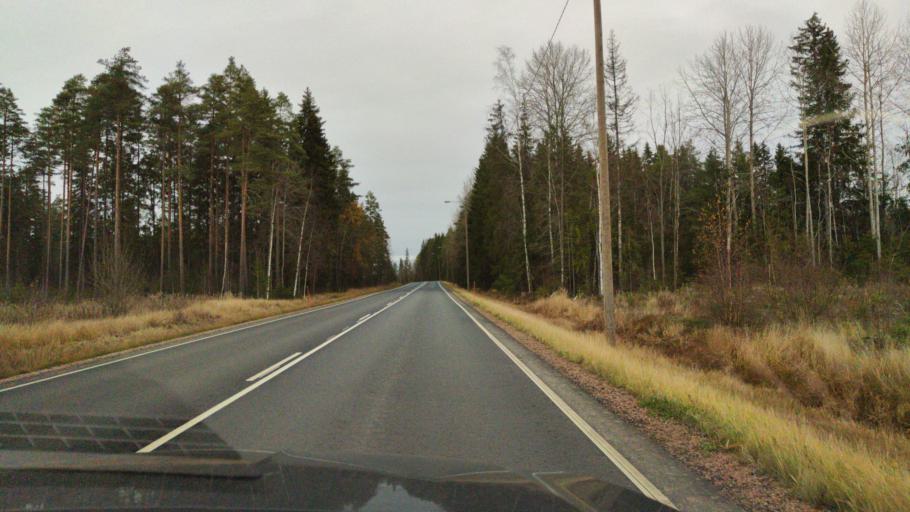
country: FI
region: Varsinais-Suomi
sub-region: Turku
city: Vahto
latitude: 60.6598
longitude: 22.4333
